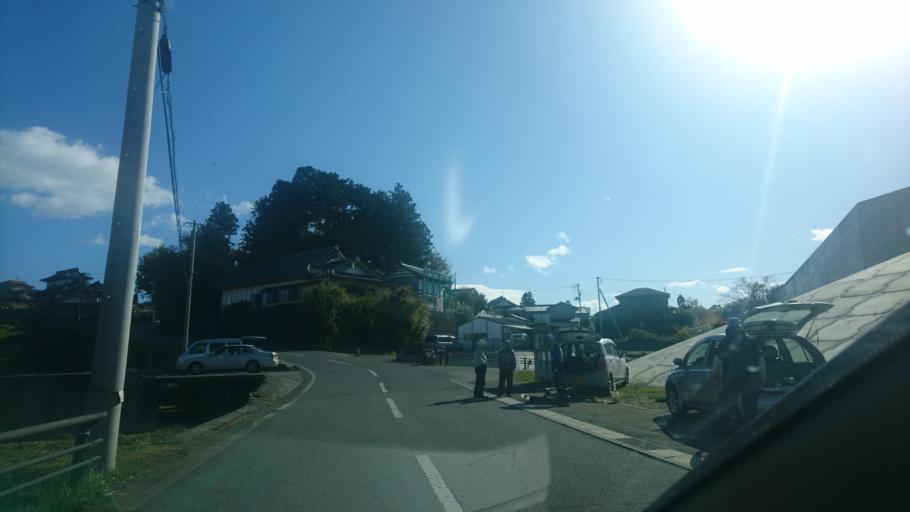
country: JP
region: Iwate
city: Ofunato
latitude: 38.9917
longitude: 141.7291
